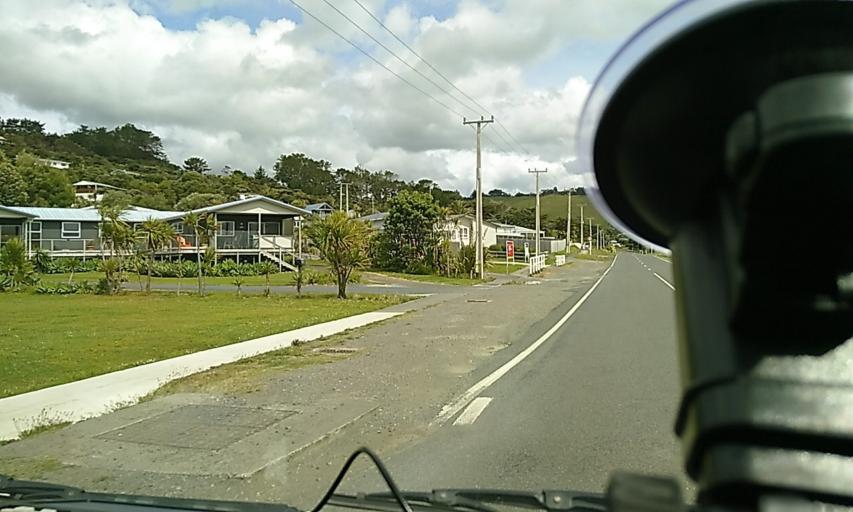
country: NZ
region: Northland
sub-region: Far North District
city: Ahipara
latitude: -35.5218
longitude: 173.3887
